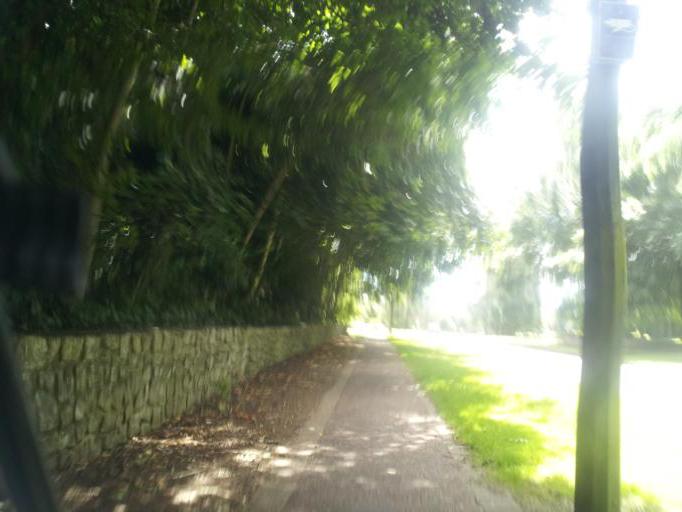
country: GB
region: England
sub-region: Kent
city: Kings Hill
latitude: 51.2803
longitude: 0.4029
